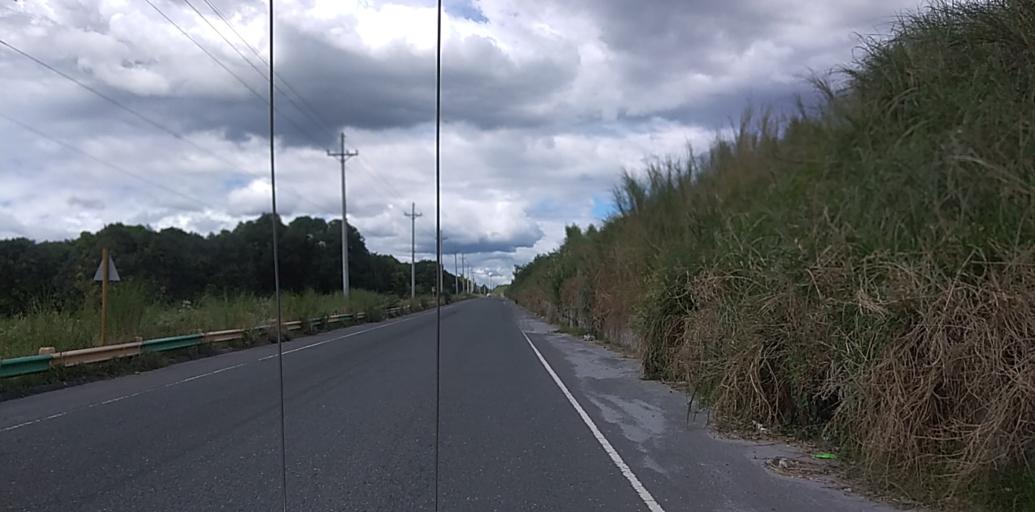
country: PH
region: Central Luzon
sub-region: Province of Pampanga
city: Dolores
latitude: 15.1007
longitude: 120.5241
